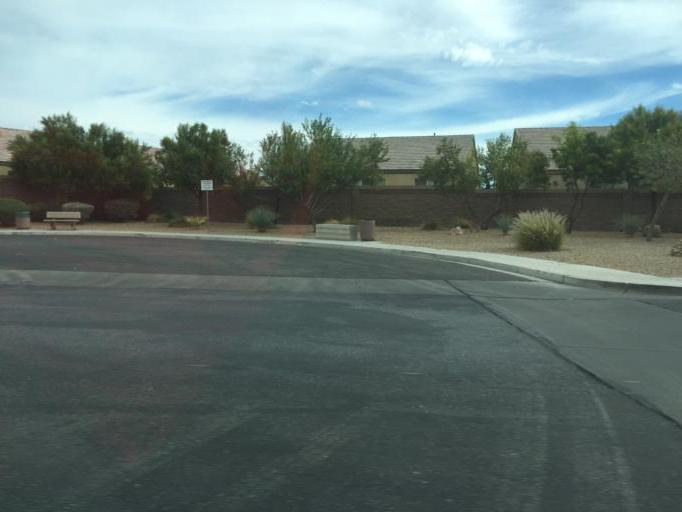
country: US
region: Nevada
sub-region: Clark County
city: Whitney
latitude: 36.1248
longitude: -115.0379
